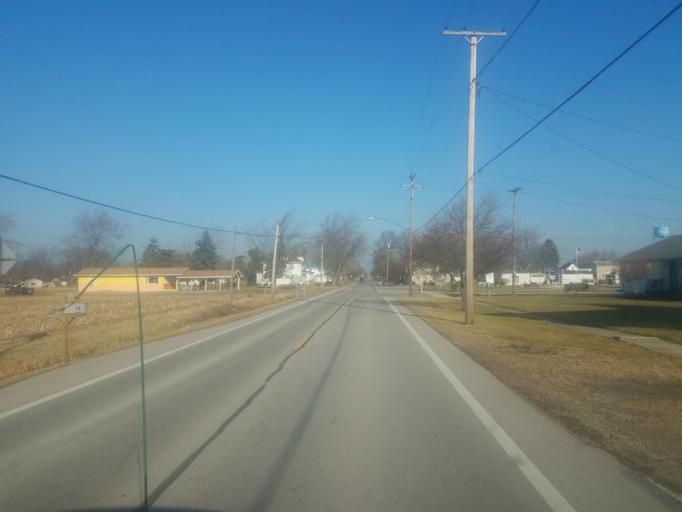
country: US
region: Ohio
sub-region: Seneca County
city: Tiffin
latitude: 41.0471
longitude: -83.0154
